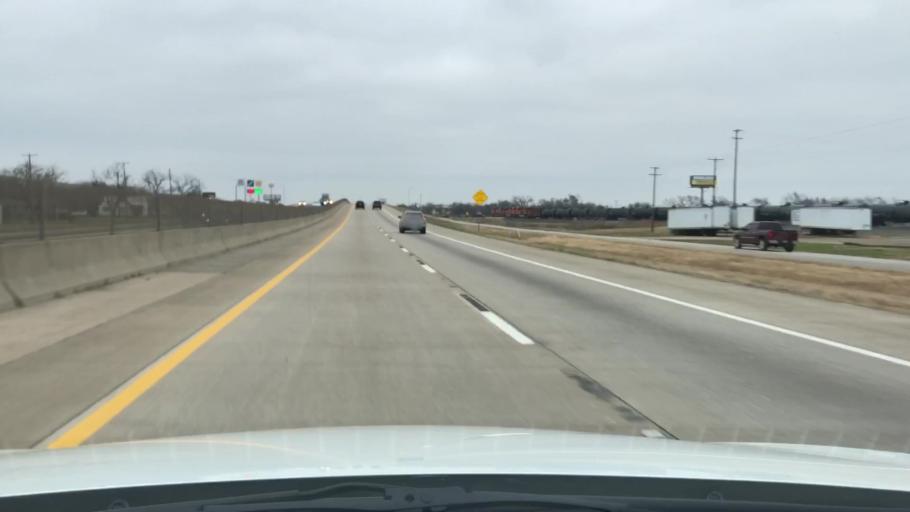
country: US
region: Texas
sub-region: Denton County
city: Sanger
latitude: 33.4846
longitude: -97.1621
